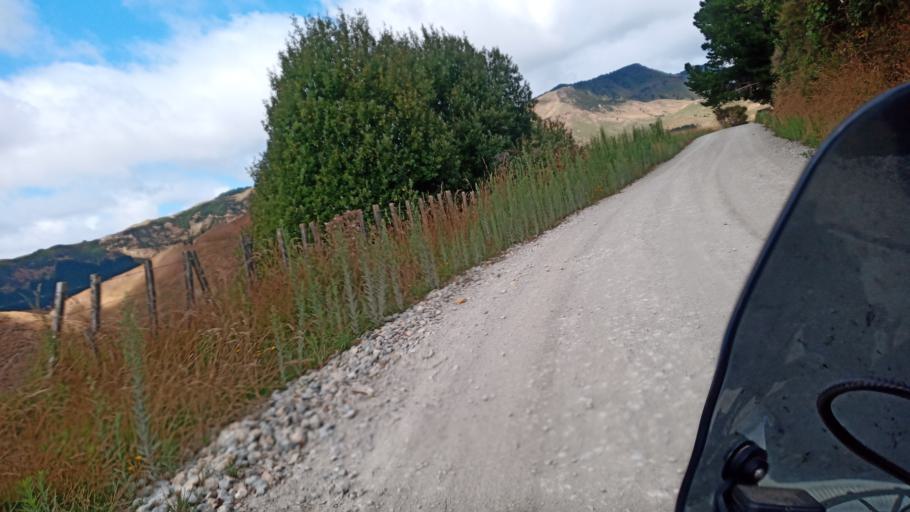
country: NZ
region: Hawke's Bay
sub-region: Wairoa District
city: Wairoa
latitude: -38.6114
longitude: 177.4383
